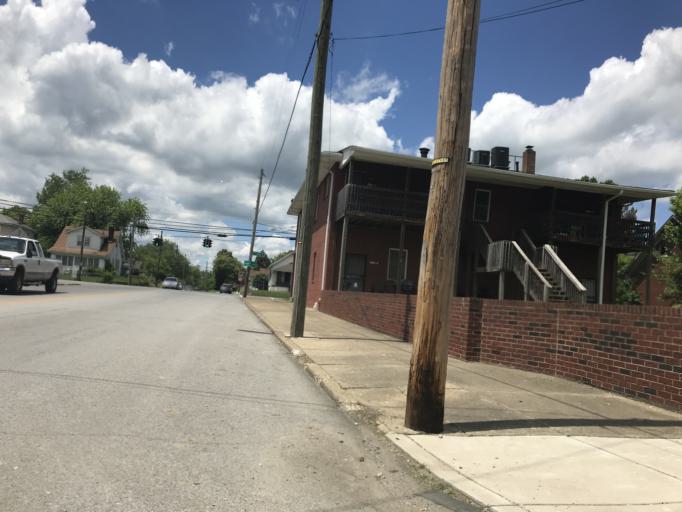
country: US
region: Kentucky
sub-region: Jefferson County
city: Shively
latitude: 38.2413
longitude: -85.8209
